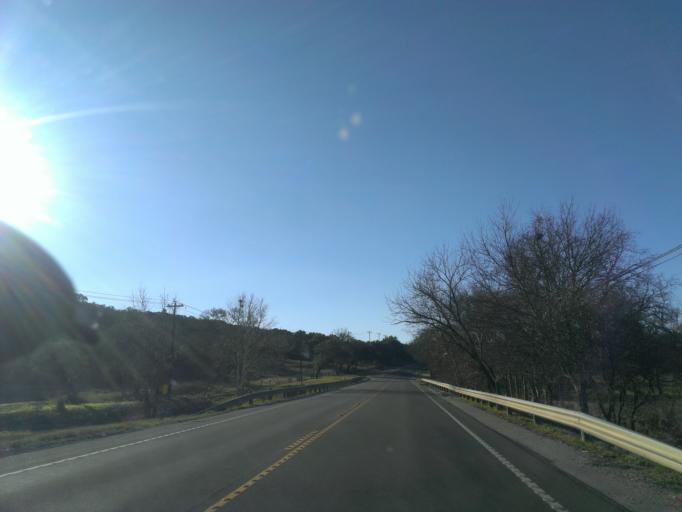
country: US
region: Texas
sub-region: Hays County
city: Dripping Springs
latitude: 30.1409
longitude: -98.0886
